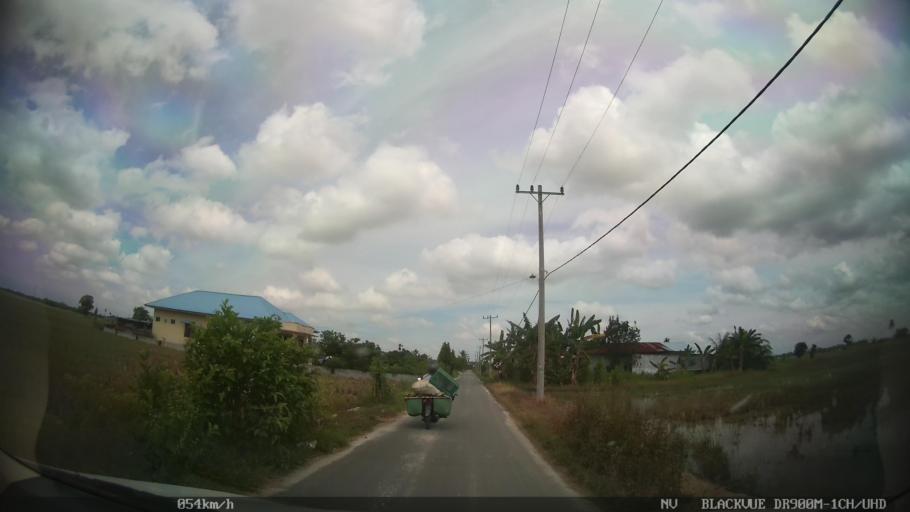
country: ID
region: North Sumatra
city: Percut
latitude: 3.5722
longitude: 98.8442
